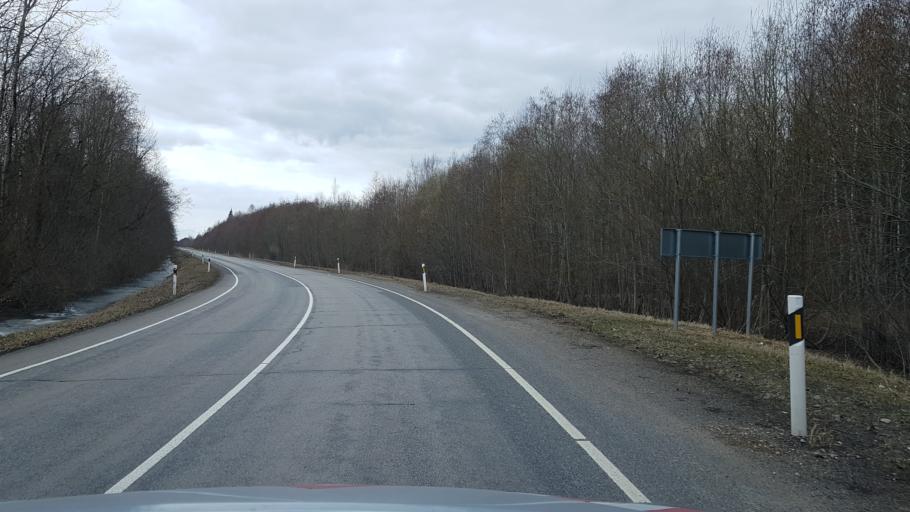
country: EE
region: Ida-Virumaa
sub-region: Narva linn
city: Narva
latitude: 59.3534
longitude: 28.0943
